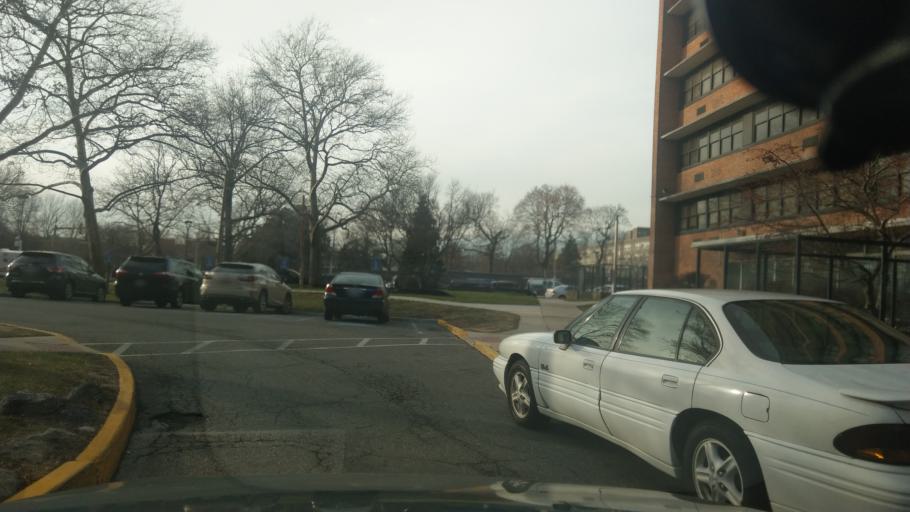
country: US
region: Pennsylvania
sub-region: Montgomery County
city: Wyncote
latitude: 40.0369
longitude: -75.1438
